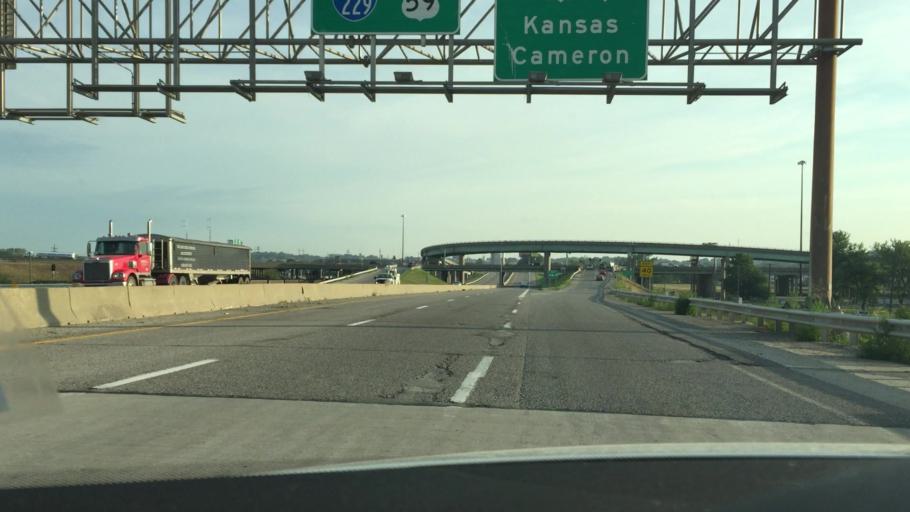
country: US
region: Kansas
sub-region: Doniphan County
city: Elwood
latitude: 39.7458
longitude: -94.8534
